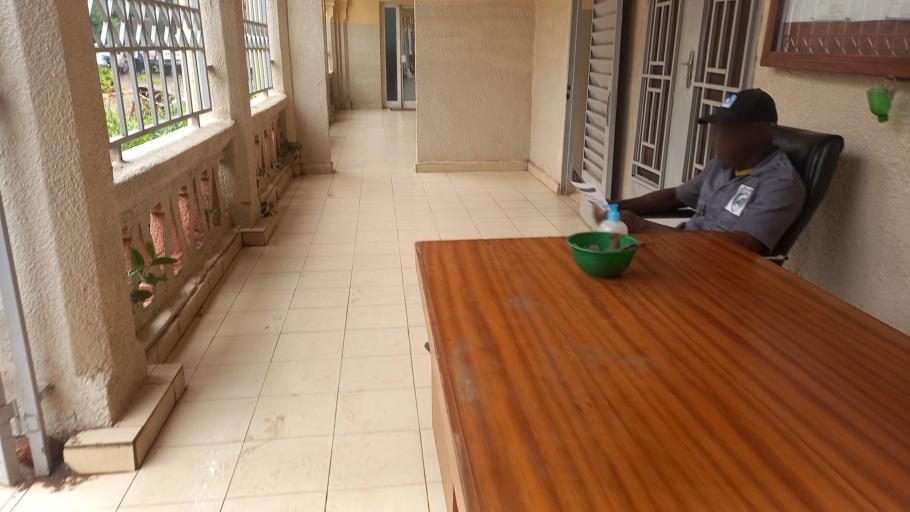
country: ML
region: Bamako
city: Bamako
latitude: 12.6493
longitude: -8.0011
